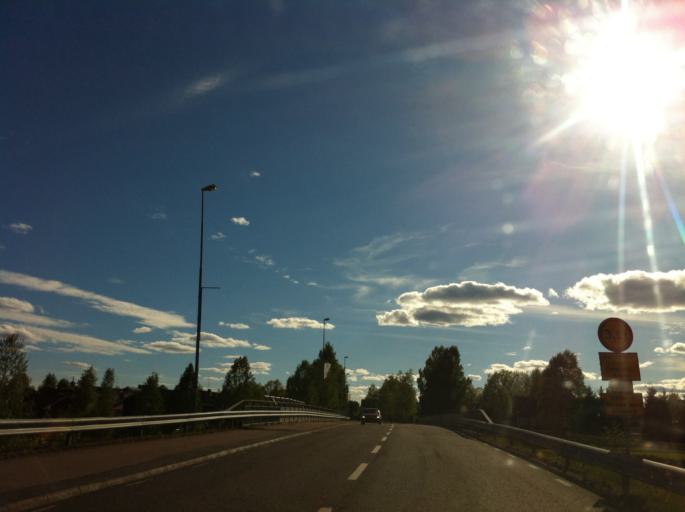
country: SE
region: Dalarna
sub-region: Leksand Municipality
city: Leksand
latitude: 60.7359
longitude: 15.0028
